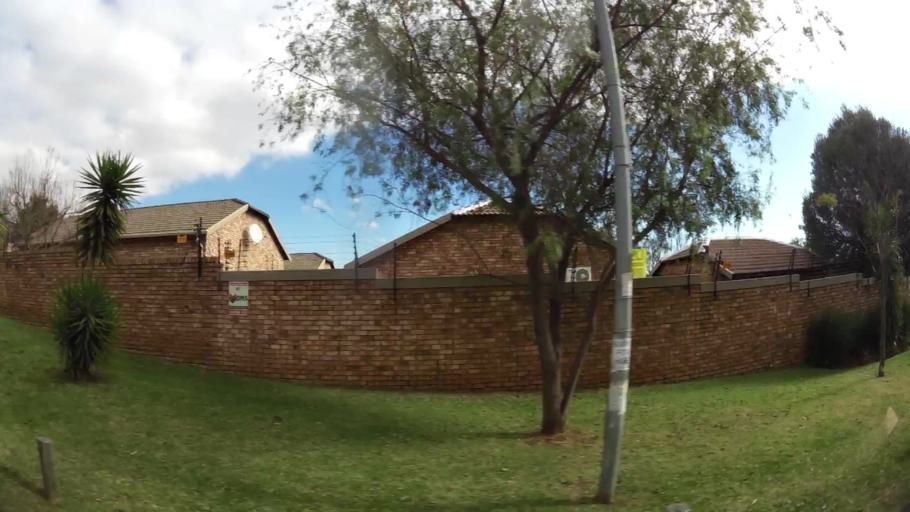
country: ZA
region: Gauteng
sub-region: City of Johannesburg Metropolitan Municipality
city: Roodepoort
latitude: -26.0984
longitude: 27.8705
